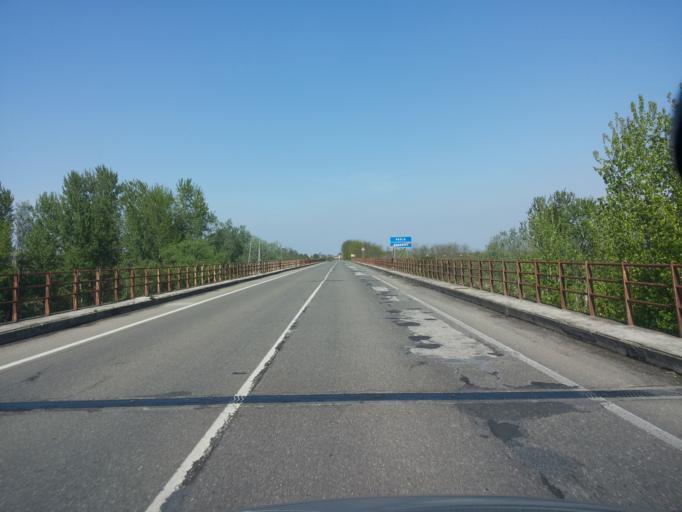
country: IT
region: Lombardy
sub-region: Provincia di Pavia
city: Langosco
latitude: 45.2069
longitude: 8.5447
